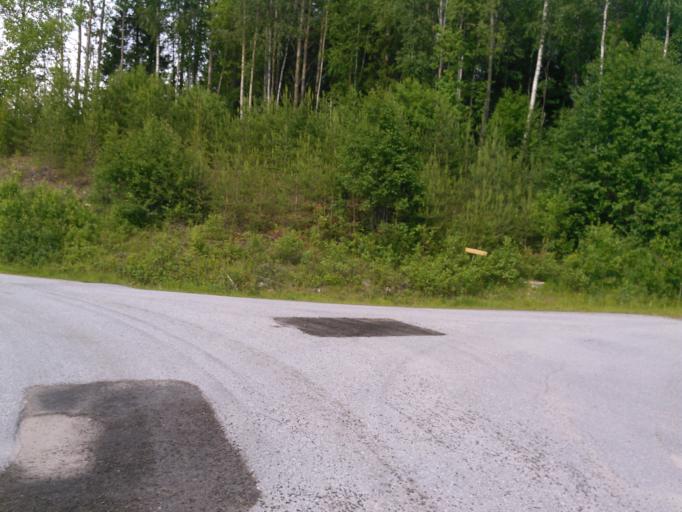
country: SE
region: Vaesterbotten
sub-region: Vannas Kommun
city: Vannasby
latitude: 63.8937
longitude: 19.9756
